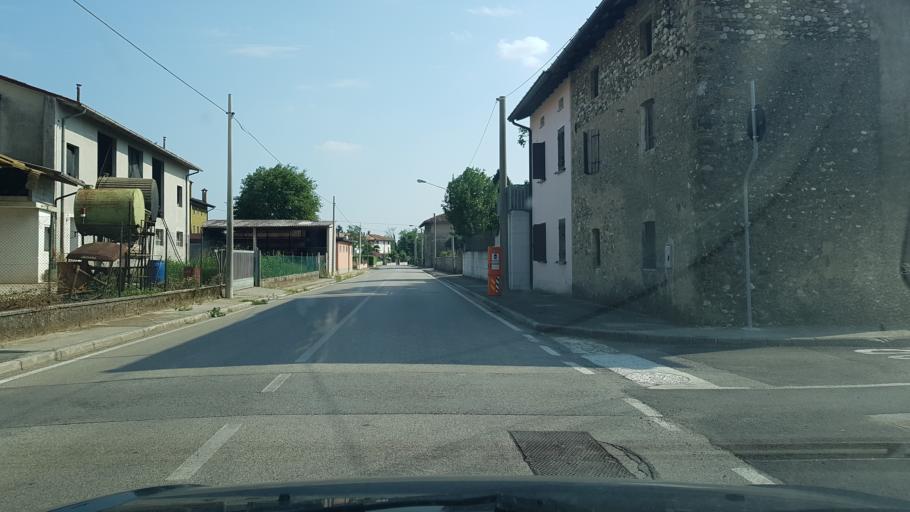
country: IT
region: Friuli Venezia Giulia
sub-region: Provincia di Udine
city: San Vito di Fagagna
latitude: 46.0885
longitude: 13.0691
